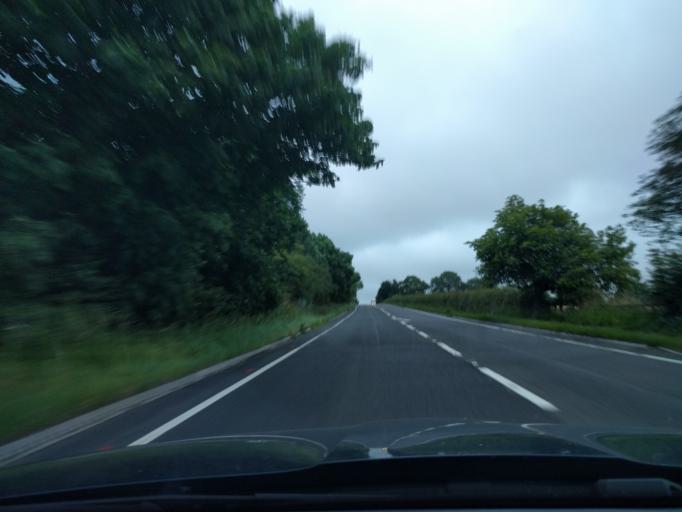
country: GB
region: England
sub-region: Northumberland
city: Felton
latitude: 55.2328
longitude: -1.7045
